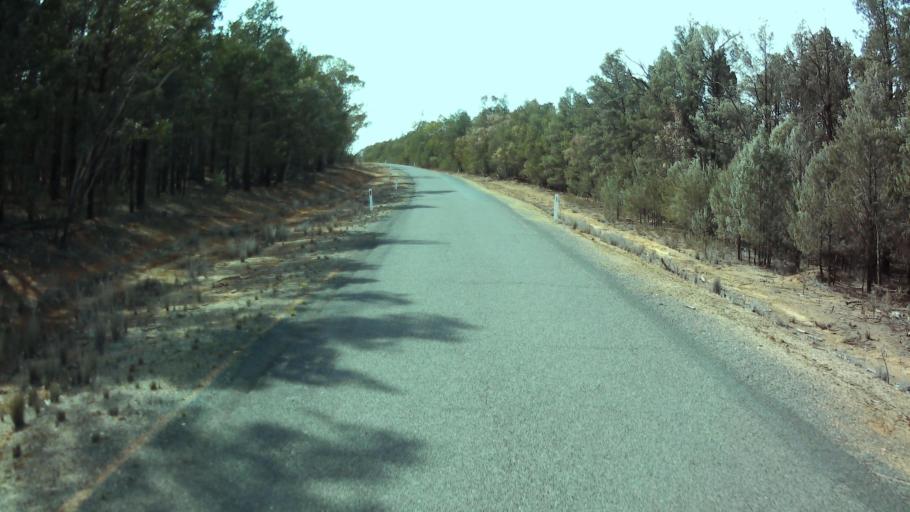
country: AU
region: New South Wales
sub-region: Weddin
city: Grenfell
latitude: -33.7409
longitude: 148.0483
